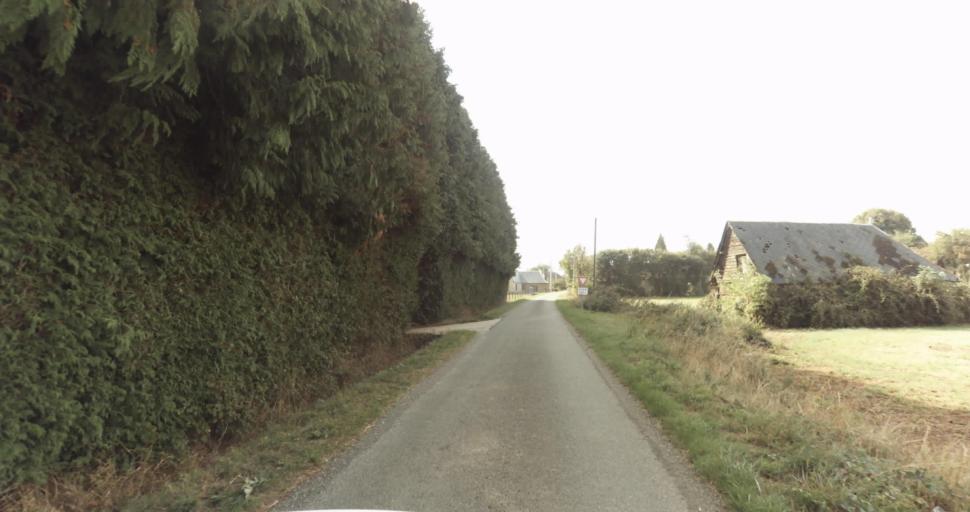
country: FR
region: Lower Normandy
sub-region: Departement de l'Orne
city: Gace
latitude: 48.8268
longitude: 0.3934
